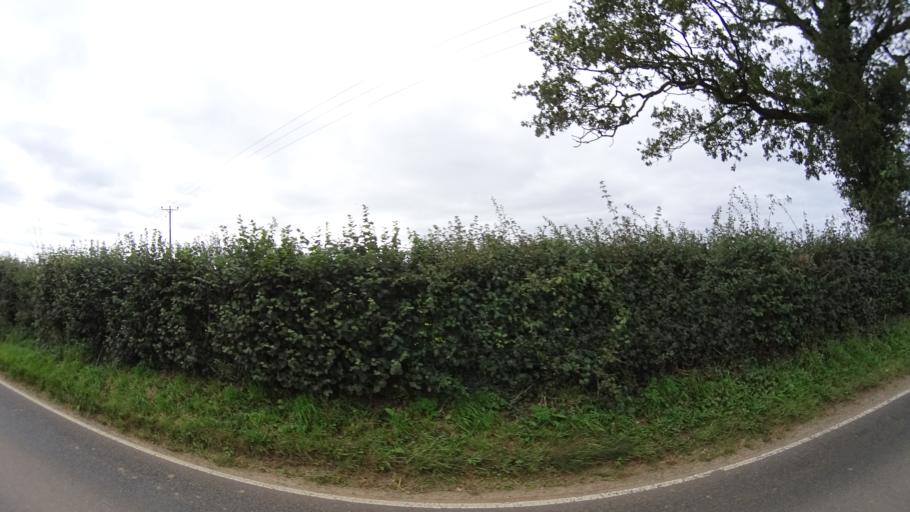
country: GB
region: England
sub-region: Dorset
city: Gillingham
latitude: 51.0473
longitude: -2.3210
